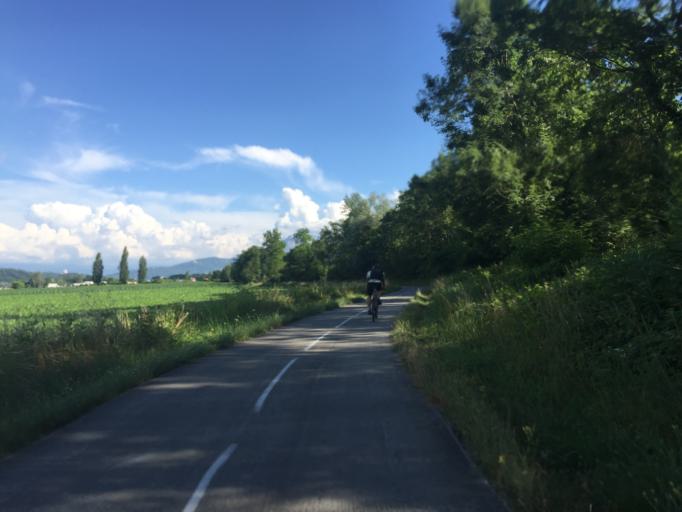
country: FR
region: Rhone-Alpes
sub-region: Departement de la Savoie
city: Le Bourget-du-Lac
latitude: 45.6334
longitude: 5.8709
